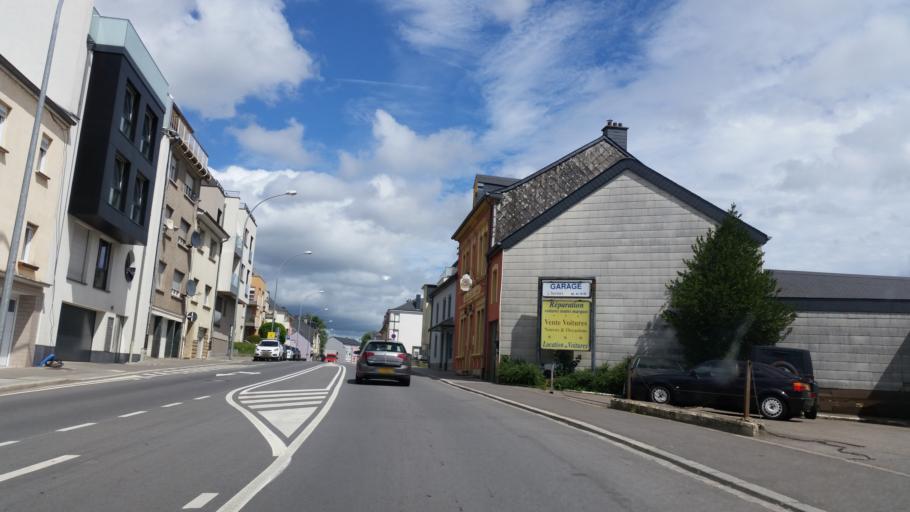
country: LU
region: Luxembourg
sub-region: Canton de Luxembourg
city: Strassen
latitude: 49.6032
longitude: 6.0915
